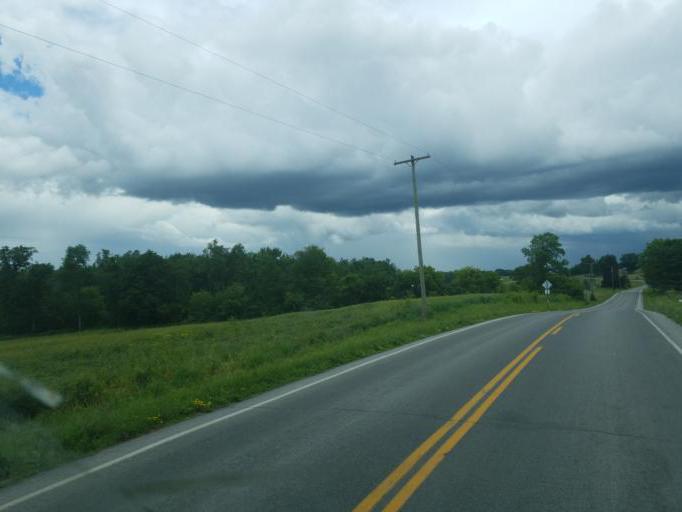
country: US
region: New York
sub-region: Wayne County
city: Clyde
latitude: 43.0327
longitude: -76.9085
